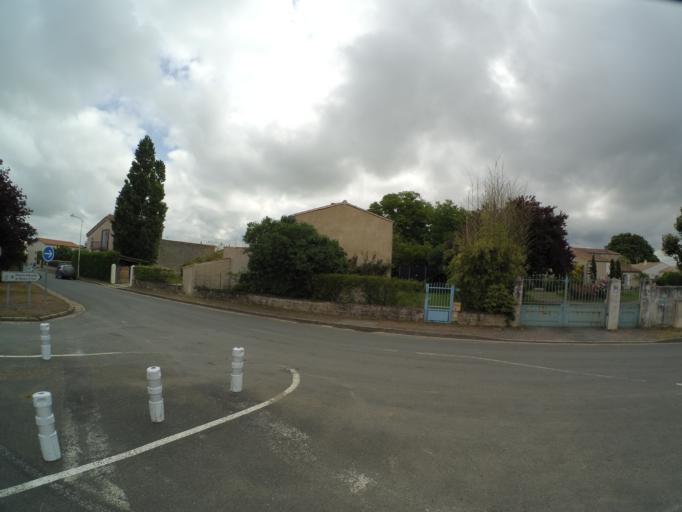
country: FR
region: Poitou-Charentes
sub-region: Departement de la Charente-Maritime
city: Yves
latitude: 46.0188
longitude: -1.0476
